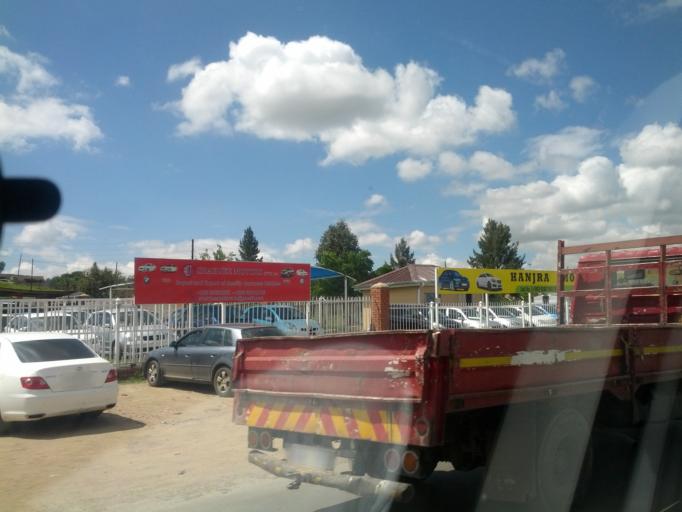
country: LS
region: Maseru
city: Maseru
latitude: -29.3004
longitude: 27.5172
